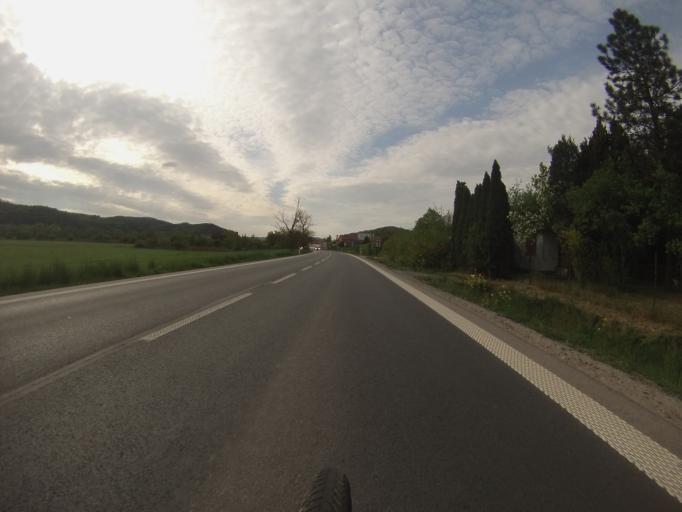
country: CZ
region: South Moravian
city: Tisnov
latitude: 49.3345
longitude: 16.4368
